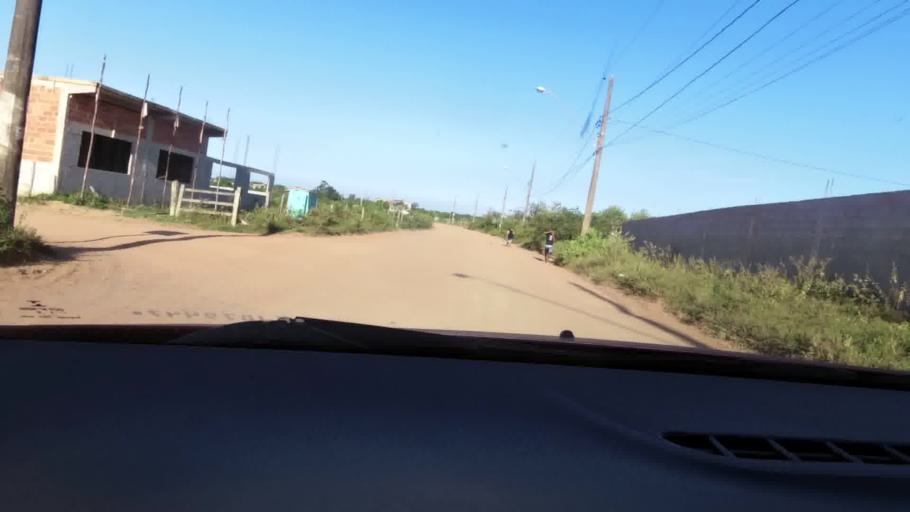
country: BR
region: Espirito Santo
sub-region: Guarapari
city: Guarapari
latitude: -20.5547
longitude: -40.4113
